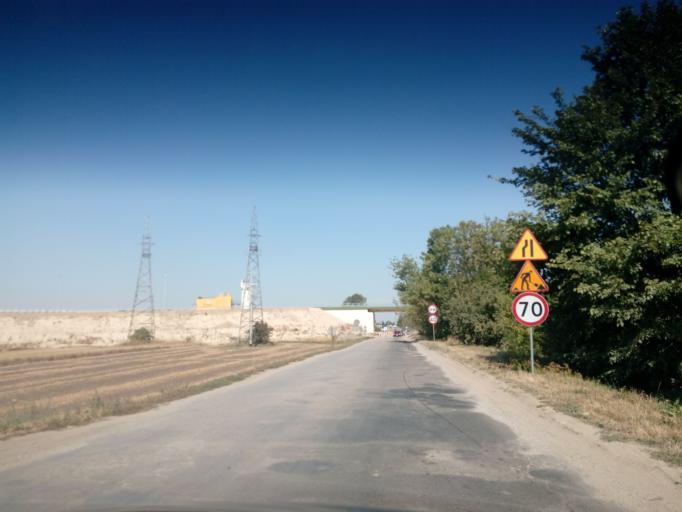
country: PL
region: Lublin Voivodeship
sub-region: Powiat hrubieszowski
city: Hrubieszow
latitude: 50.7876
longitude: 23.9011
